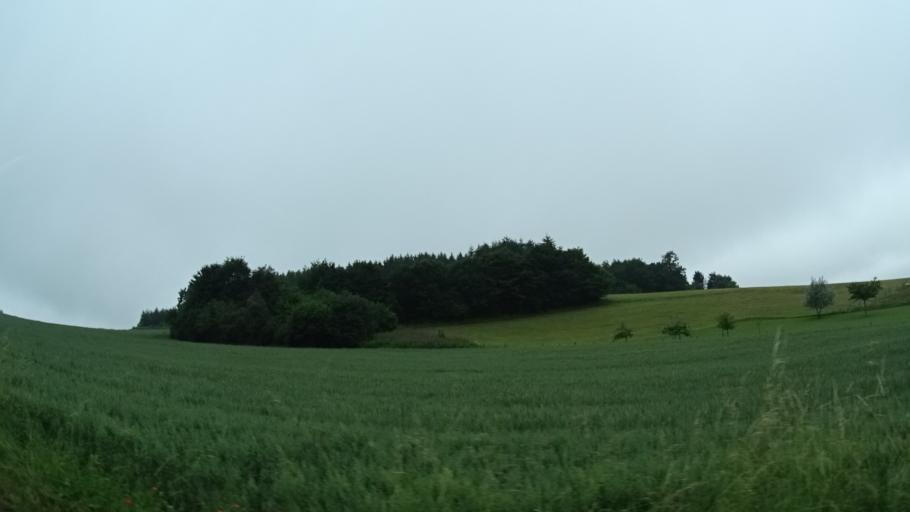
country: BE
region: Wallonia
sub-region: Province du Luxembourg
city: Leglise
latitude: 49.7964
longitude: 5.5410
